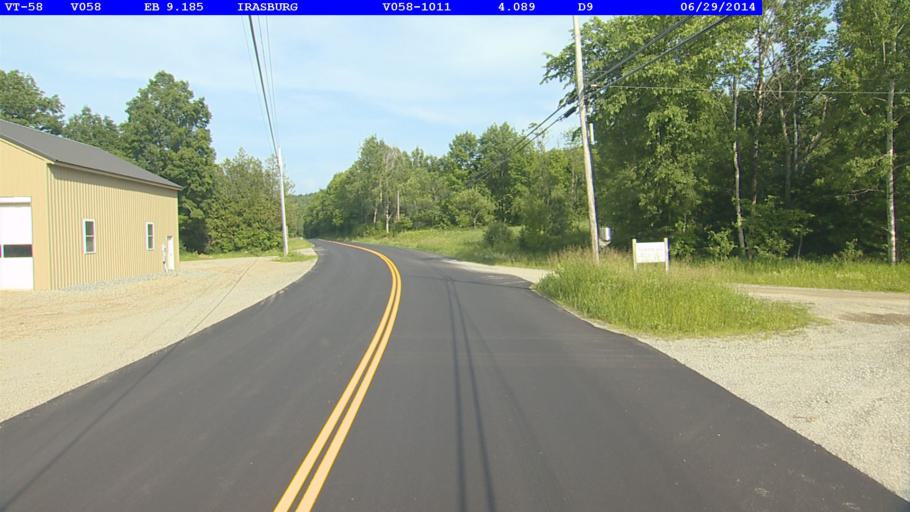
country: US
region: Vermont
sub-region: Orleans County
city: Newport
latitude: 44.8044
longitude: -72.2634
